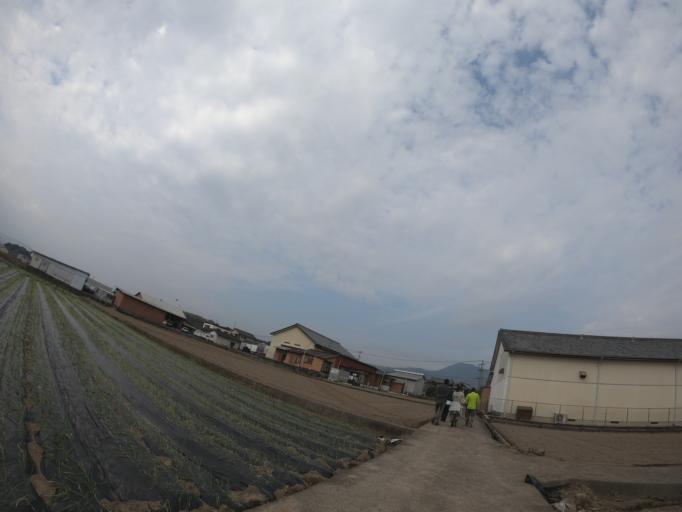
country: JP
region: Nagasaki
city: Shimabara
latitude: 32.6602
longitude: 130.3028
